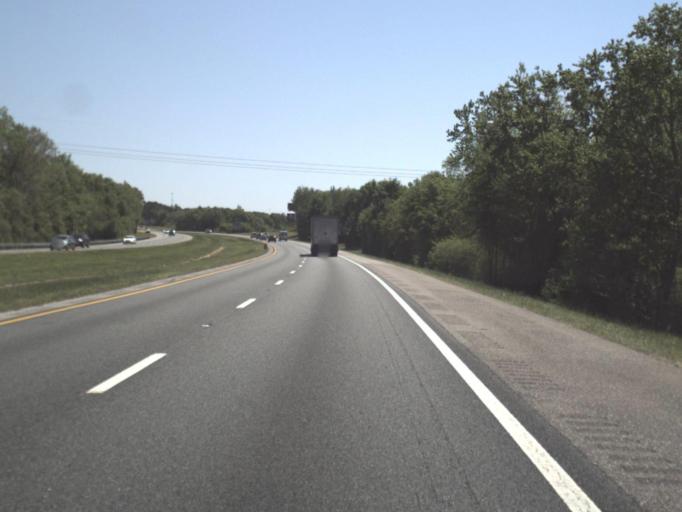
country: US
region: Florida
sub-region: Escambia County
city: Ensley
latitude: 30.5051
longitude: -87.2824
